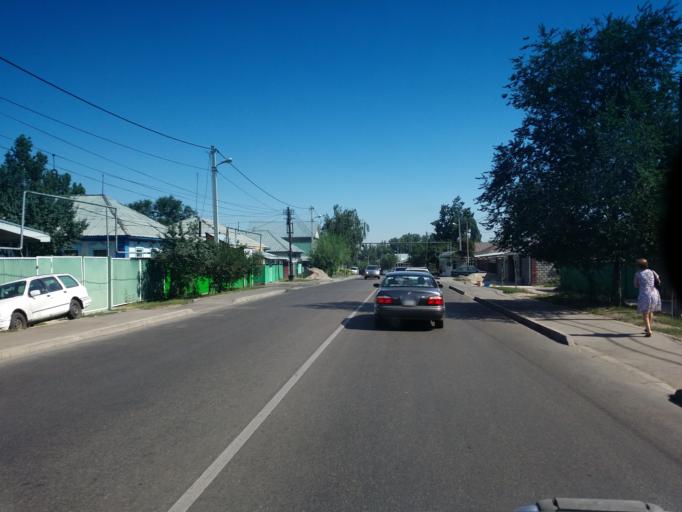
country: KZ
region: Almaty Oblysy
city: Pervomayskiy
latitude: 43.3327
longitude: 76.9337
